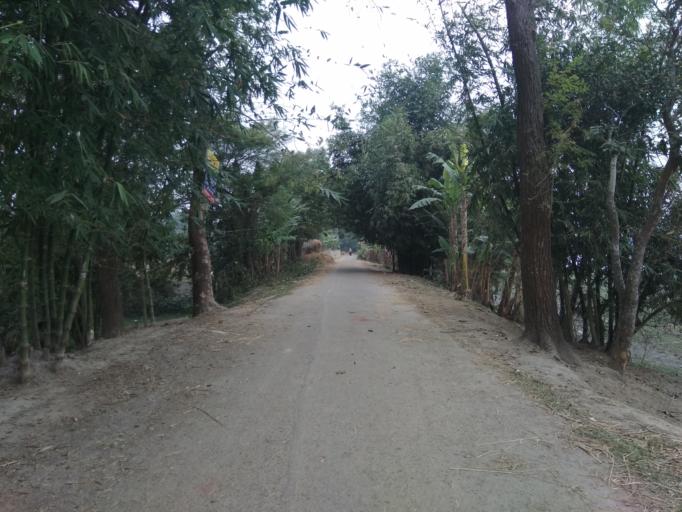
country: BD
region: Barisal
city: Mehendiganj
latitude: 22.9170
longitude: 90.3910
